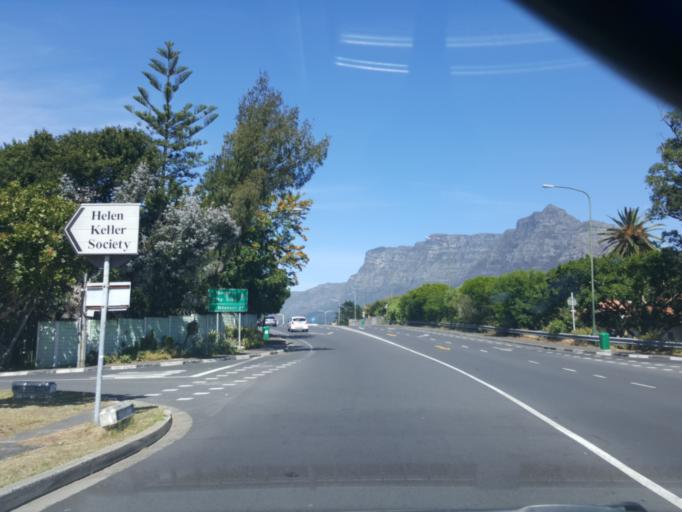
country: ZA
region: Western Cape
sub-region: City of Cape Town
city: Rosebank
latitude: -33.9442
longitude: 18.4931
